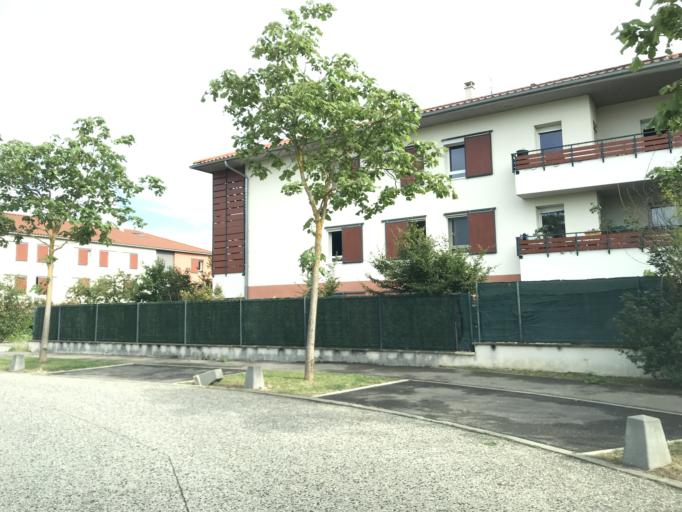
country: FR
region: Rhone-Alpes
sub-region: Departement du Rhone
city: Mions
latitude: 45.6669
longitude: 4.9535
